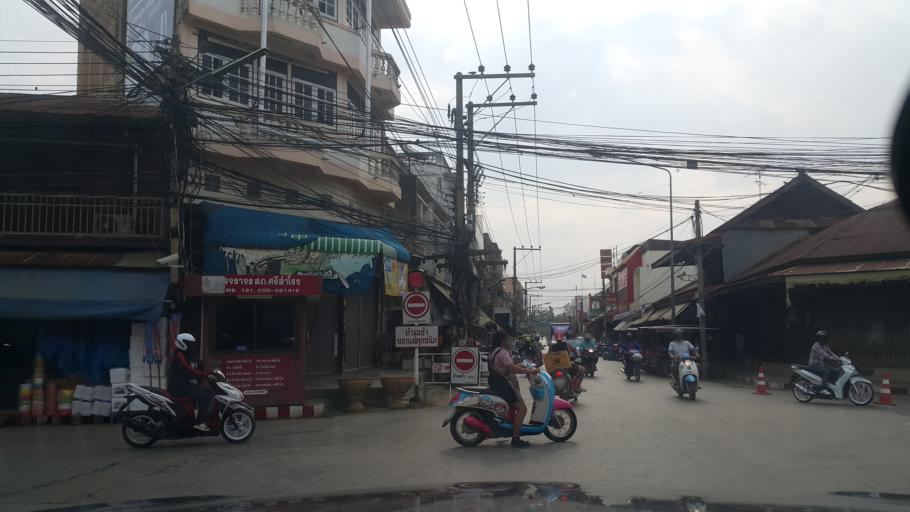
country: TH
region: Sukhothai
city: Si Samrong
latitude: 17.1680
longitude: 99.8621
